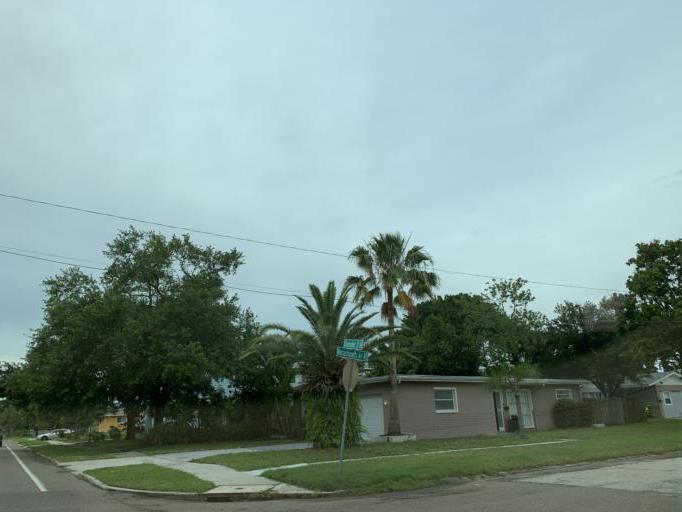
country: US
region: Florida
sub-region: Pinellas County
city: Gandy
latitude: 27.8155
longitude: -82.6025
